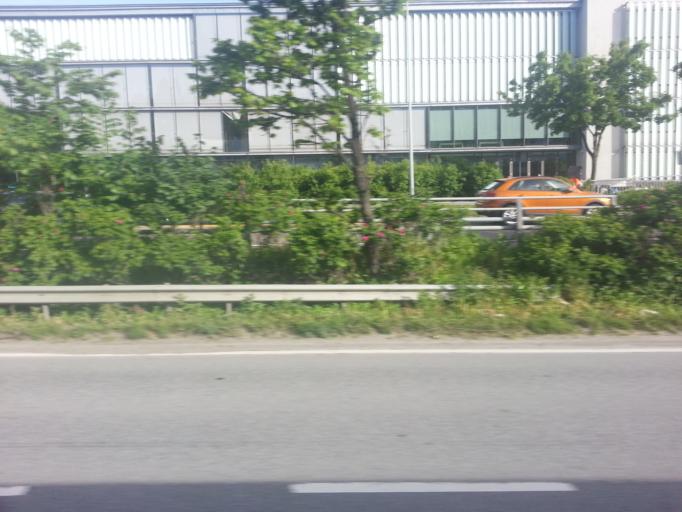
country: NO
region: Akershus
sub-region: Baerum
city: Lysaker
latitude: 59.9113
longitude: 10.6314
